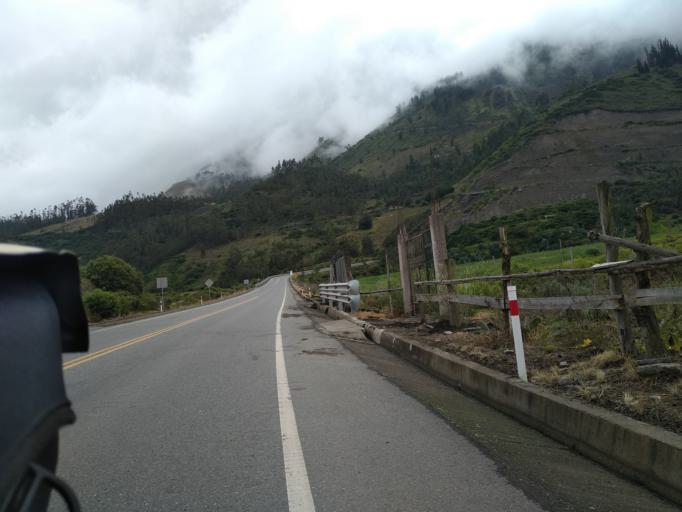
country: EC
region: Tungurahua
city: Banos
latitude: -1.5049
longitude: -78.5213
